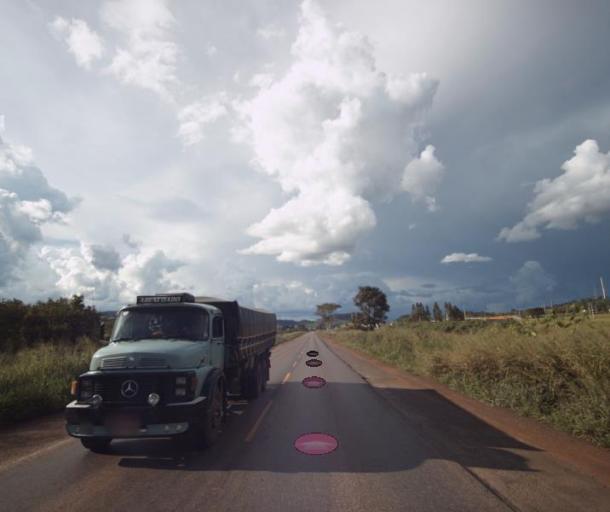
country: BR
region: Goias
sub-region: Rialma
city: Rialma
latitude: -15.3070
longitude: -49.5714
